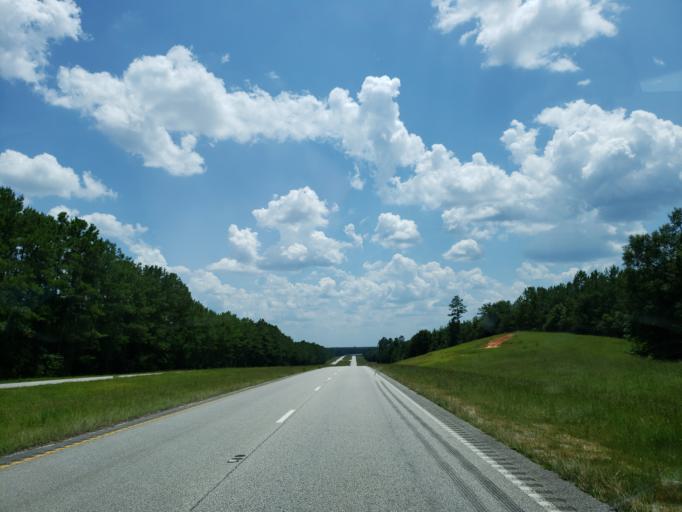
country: US
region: Mississippi
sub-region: Greene County
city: Leakesville
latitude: 31.3097
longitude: -88.4996
